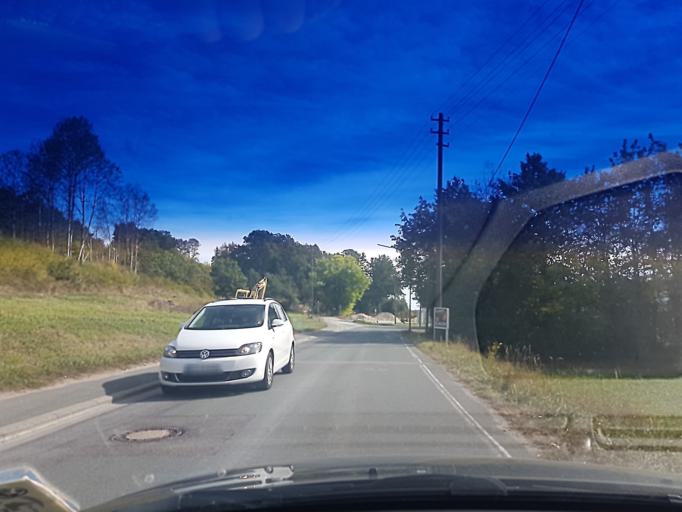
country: DE
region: Bavaria
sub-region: Regierungsbezirk Mittelfranken
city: Wachenroth
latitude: 49.7836
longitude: 10.7004
